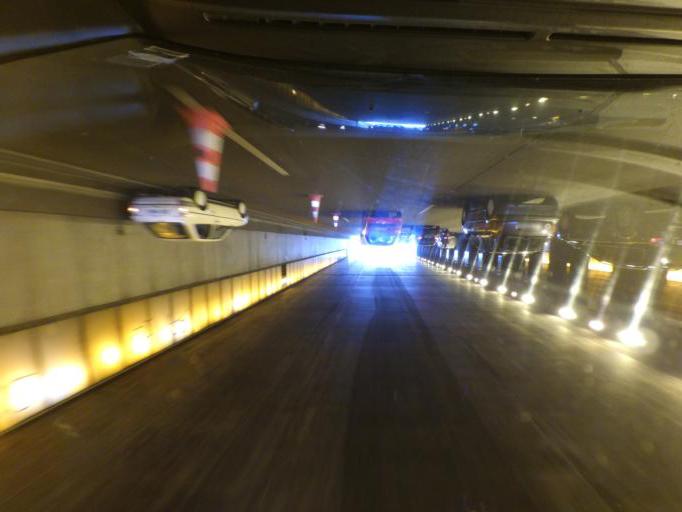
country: FR
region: Ile-de-France
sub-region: Departement des Hauts-de-Seine
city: Neuilly-sur-Seine
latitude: 48.8726
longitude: 2.2743
